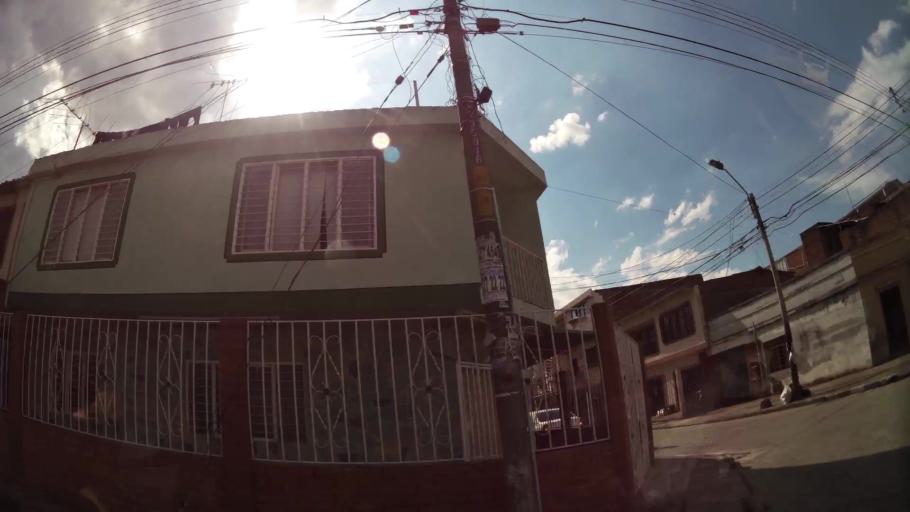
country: CO
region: Valle del Cauca
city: Cali
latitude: 3.3768
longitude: -76.4898
